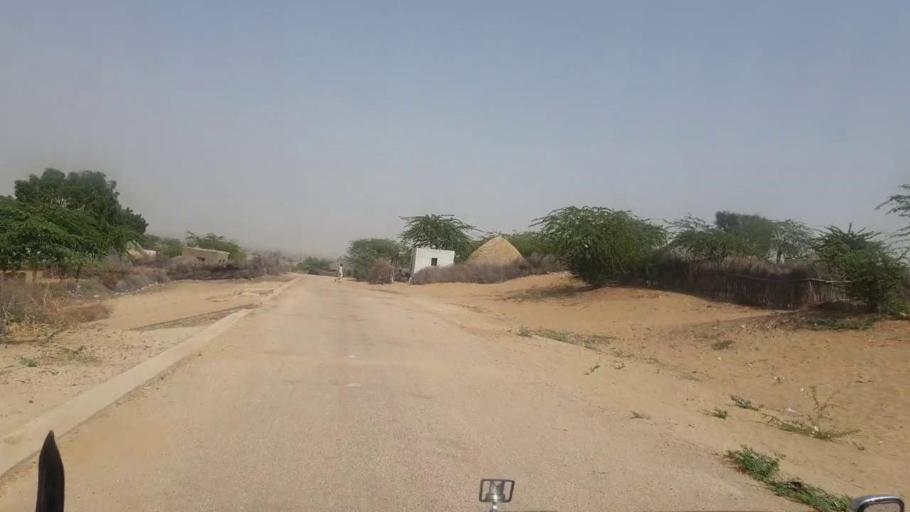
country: PK
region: Sindh
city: Umarkot
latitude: 25.2307
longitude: 70.2458
